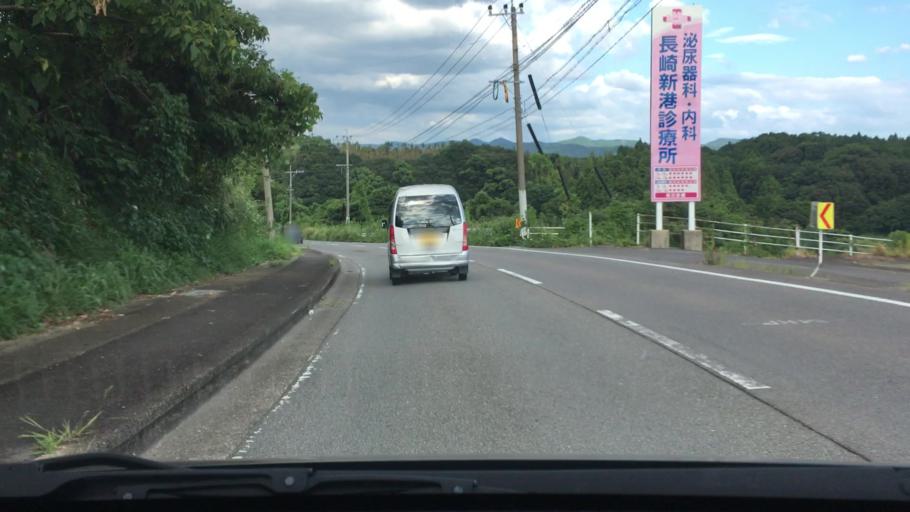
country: JP
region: Nagasaki
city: Togitsu
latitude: 32.8192
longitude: 129.7383
